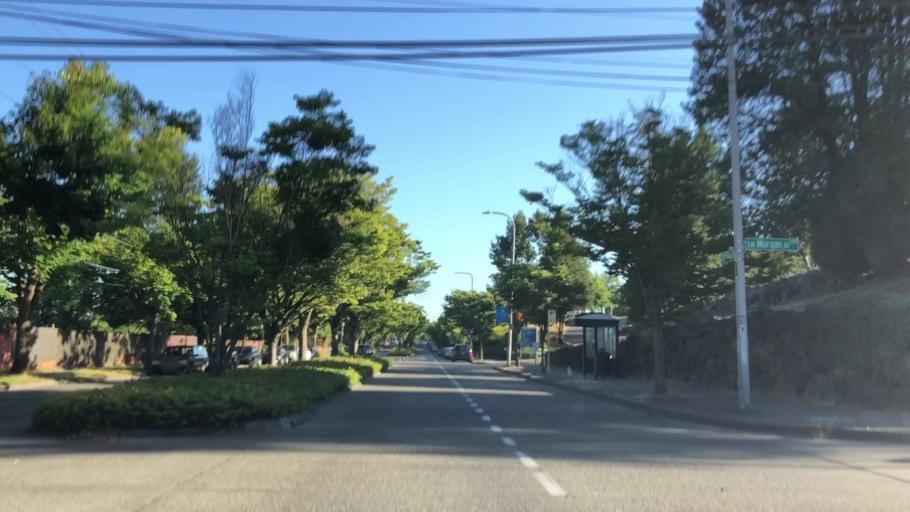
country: US
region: Washington
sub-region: King County
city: White Center
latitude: 47.5448
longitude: -122.3549
